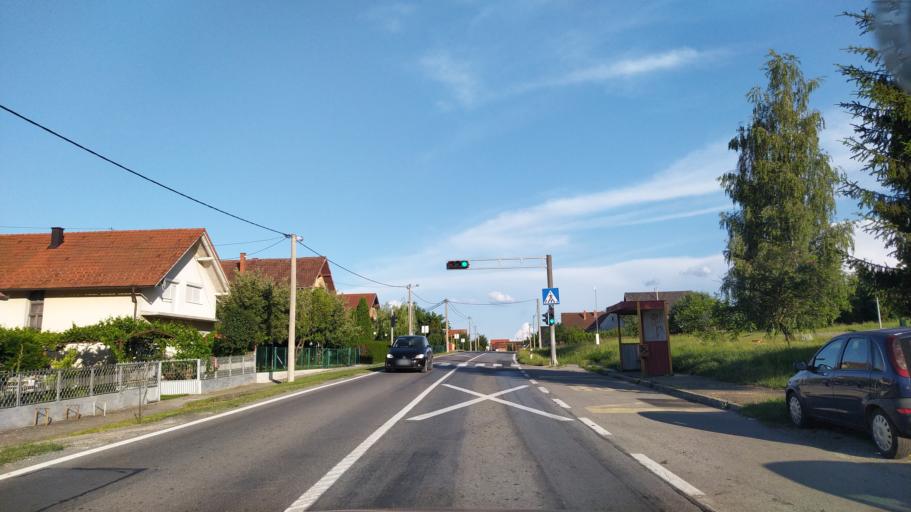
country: HR
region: Virovitick-Podravska
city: Slatina
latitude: 45.6887
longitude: 17.7323
